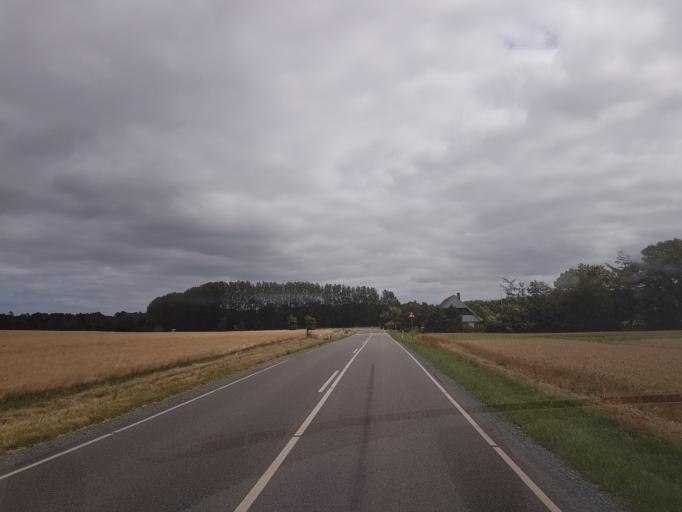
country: DK
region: South Denmark
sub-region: Nordfyns Kommune
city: Bogense
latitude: 55.5681
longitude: 10.1861
